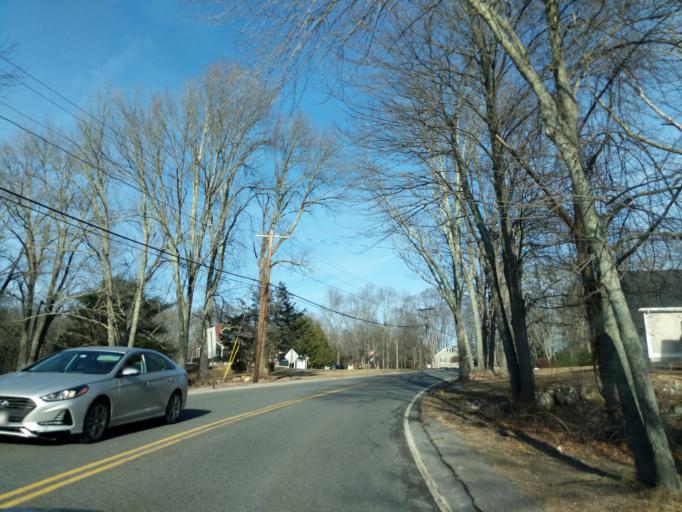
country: US
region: Massachusetts
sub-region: Worcester County
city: Blackstone
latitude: 42.0336
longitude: -71.5382
